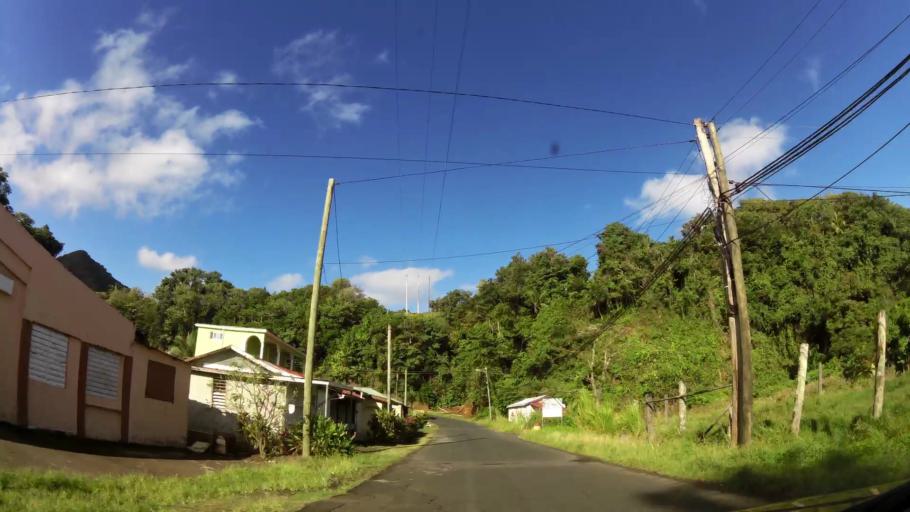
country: DM
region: Saint Andrew
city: Calibishie
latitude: 15.5929
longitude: -61.3796
